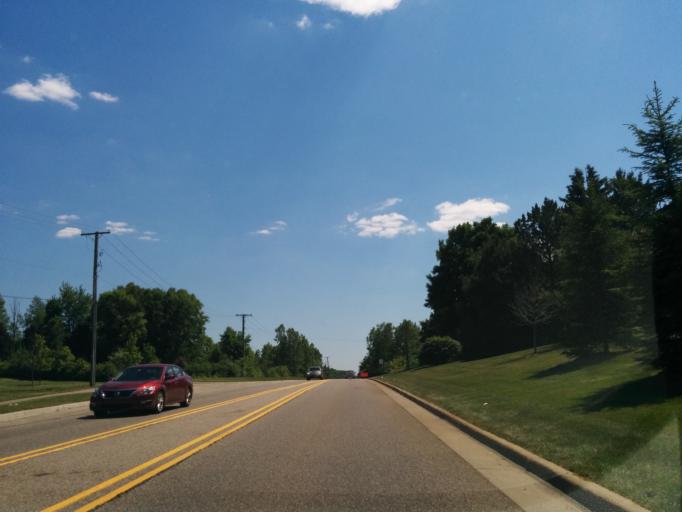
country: US
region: Michigan
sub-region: Oakland County
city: West Bloomfield Township
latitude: 42.5400
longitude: -83.3802
